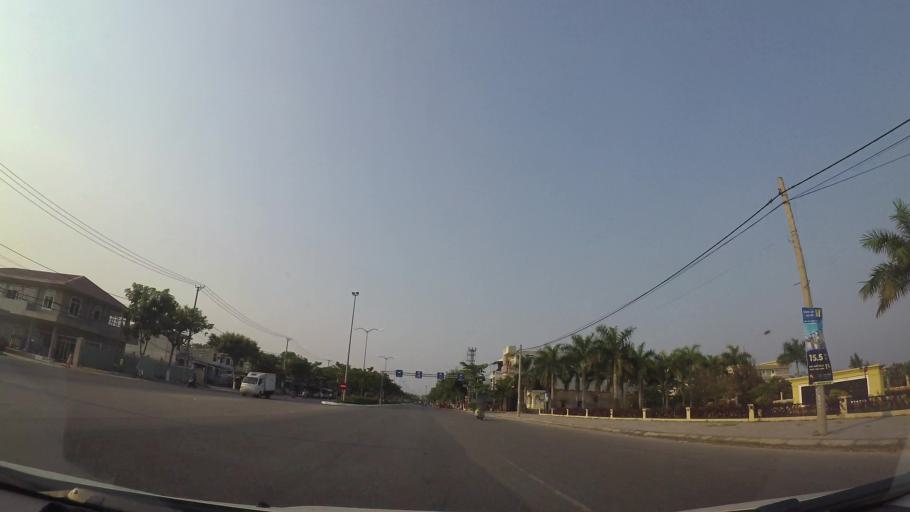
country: VN
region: Da Nang
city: Ngu Hanh Son
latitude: 15.9738
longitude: 108.2548
